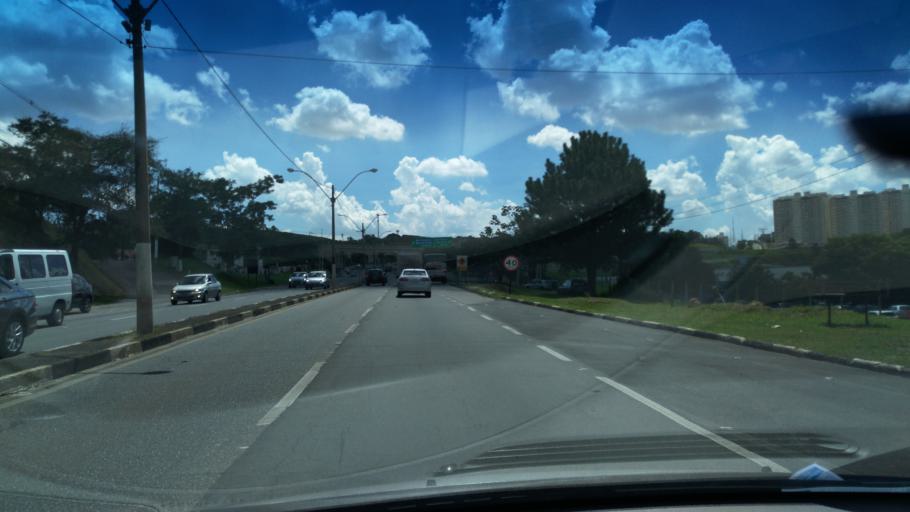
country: BR
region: Sao Paulo
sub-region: Valinhos
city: Valinhos
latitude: -22.9581
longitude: -47.0184
